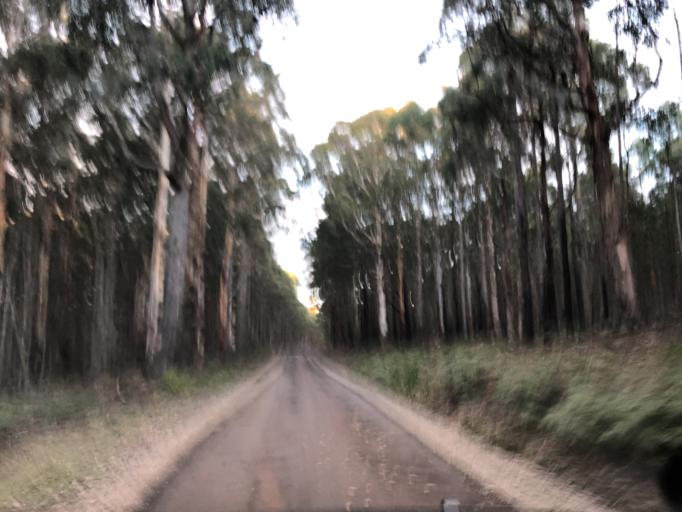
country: AU
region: Victoria
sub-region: Moorabool
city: Bacchus Marsh
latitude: -37.4358
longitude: 144.4053
